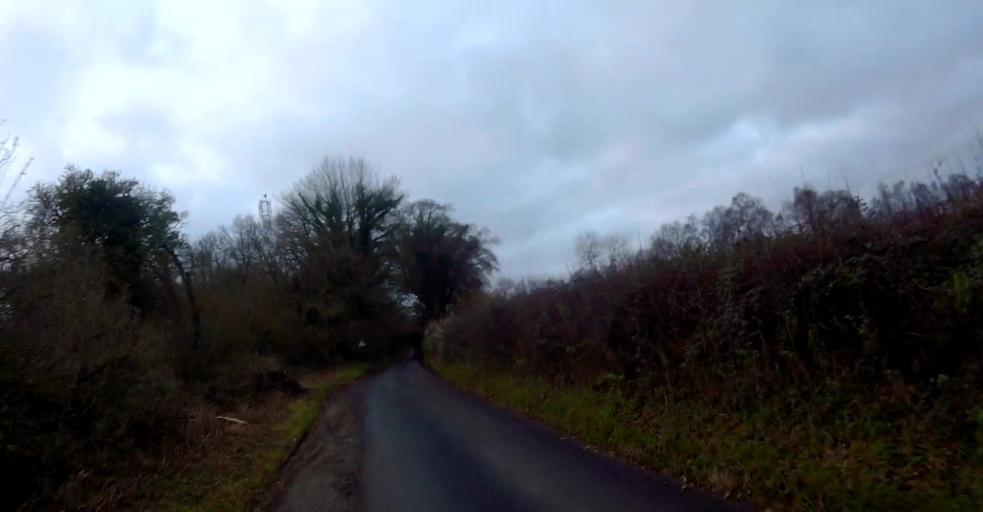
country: GB
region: England
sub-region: Hampshire
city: Overton
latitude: 51.2239
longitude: -1.2317
